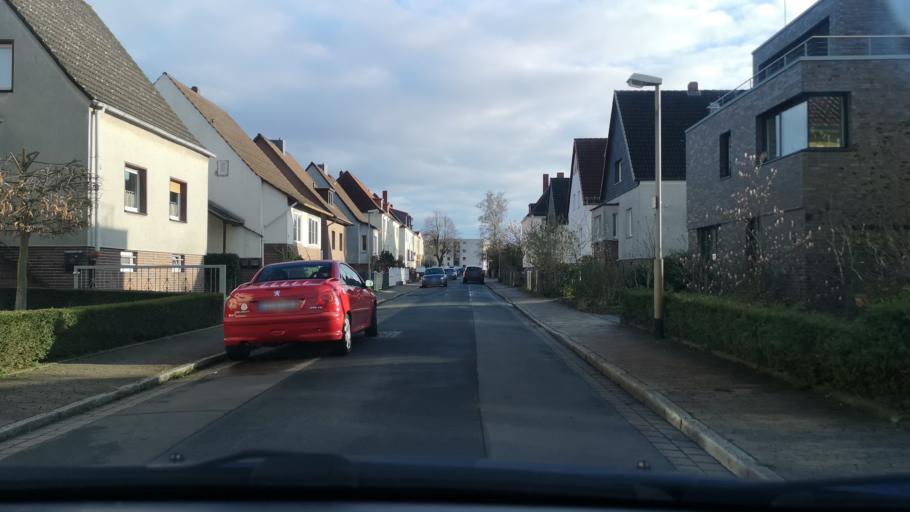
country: DE
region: Lower Saxony
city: Hannover
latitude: 52.4034
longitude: 9.6894
